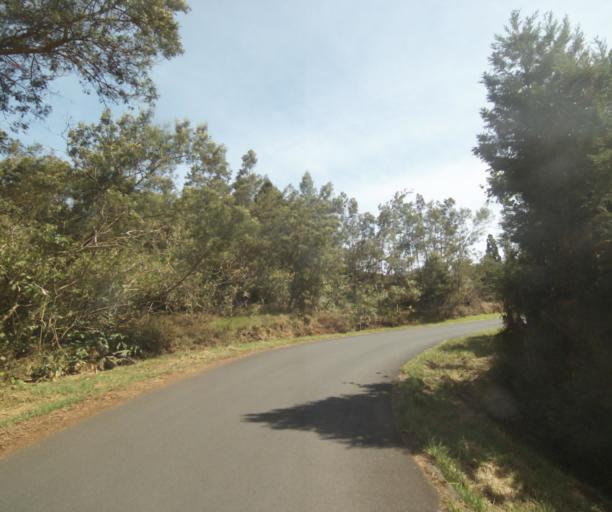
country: RE
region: Reunion
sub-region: Reunion
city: Trois-Bassins
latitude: -21.0513
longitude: 55.3522
